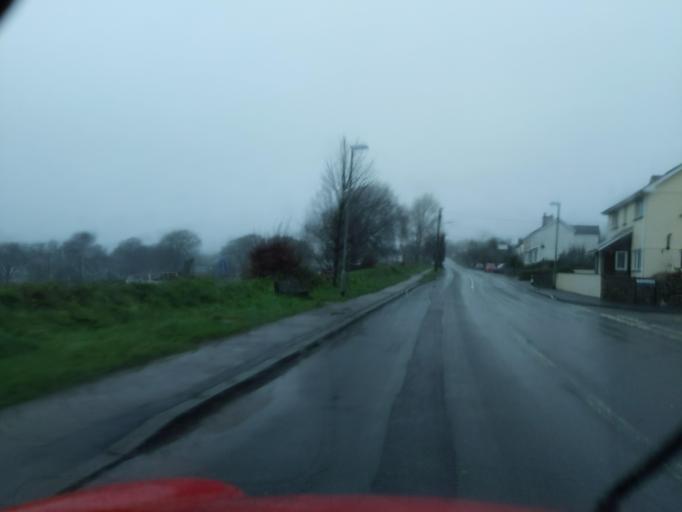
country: GB
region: England
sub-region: Cornwall
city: Callington
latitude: 50.5092
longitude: -4.3137
